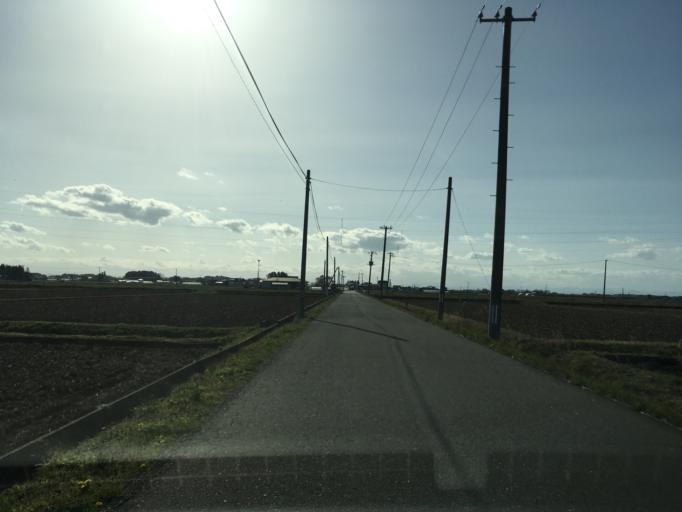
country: JP
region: Miyagi
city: Wakuya
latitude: 38.6595
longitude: 141.2275
